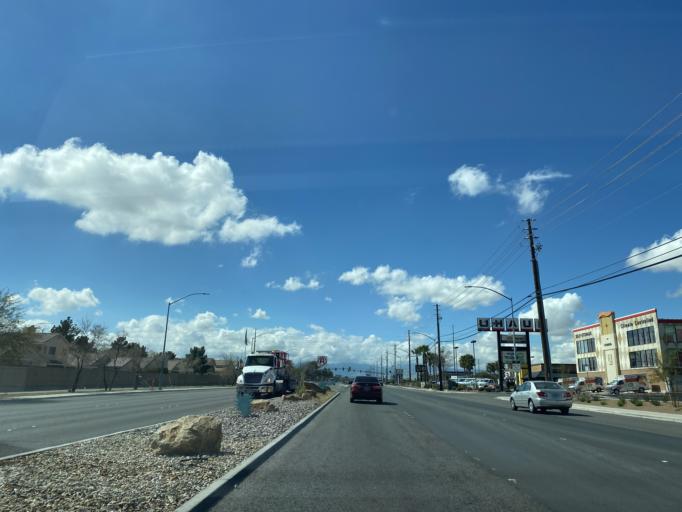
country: US
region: Nevada
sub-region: Clark County
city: North Las Vegas
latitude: 36.2396
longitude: -115.1405
